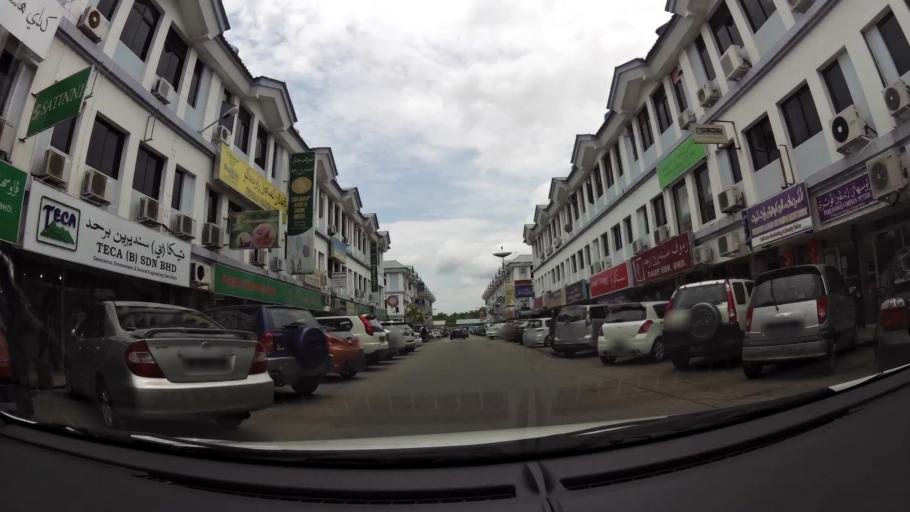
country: BN
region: Brunei and Muara
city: Bandar Seri Begawan
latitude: 4.9165
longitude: 114.9131
